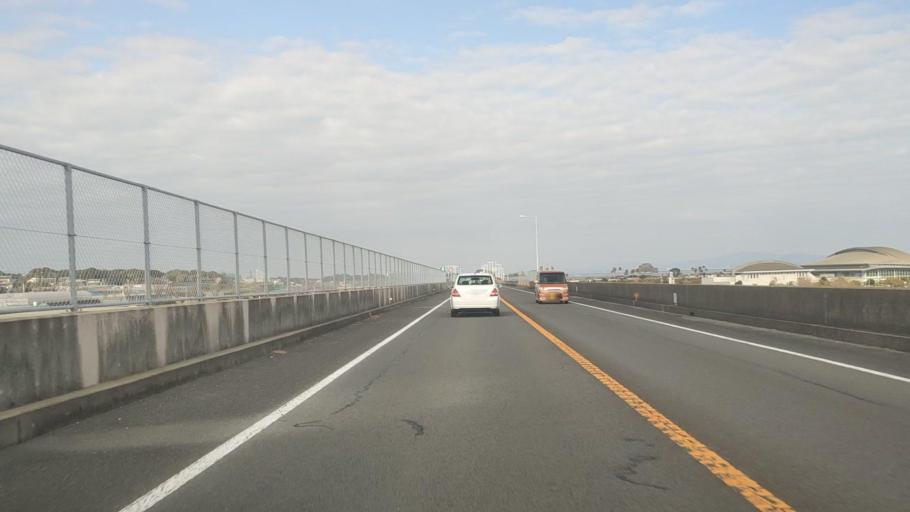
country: JP
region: Nagasaki
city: Shimabara
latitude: 32.7415
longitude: 130.3717
